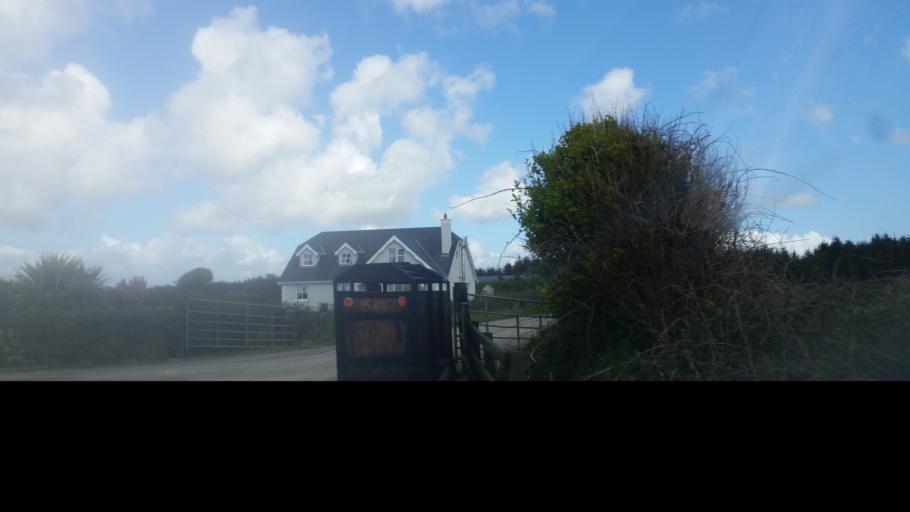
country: IE
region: Munster
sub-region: Waterford
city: Dunmore East
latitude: 52.1977
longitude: -6.8994
